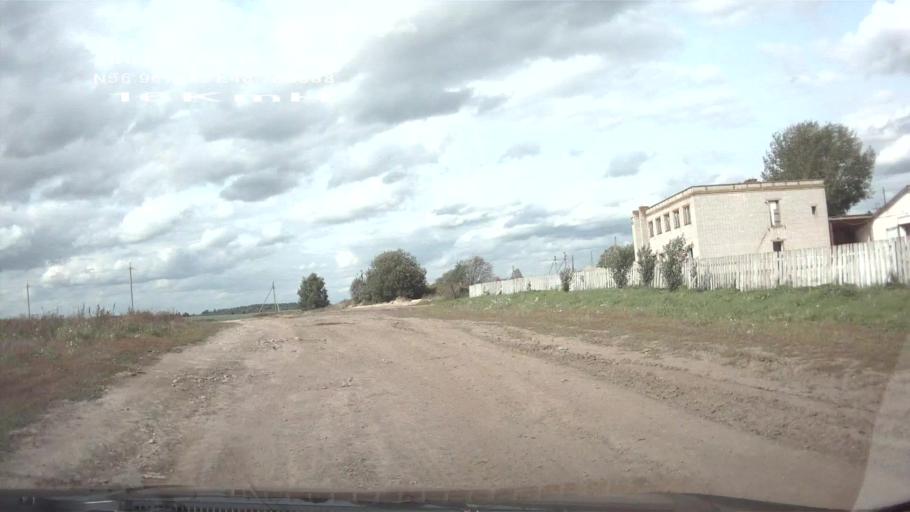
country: RU
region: Mariy-El
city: Kuzhener
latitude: 56.9675
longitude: 48.7857
